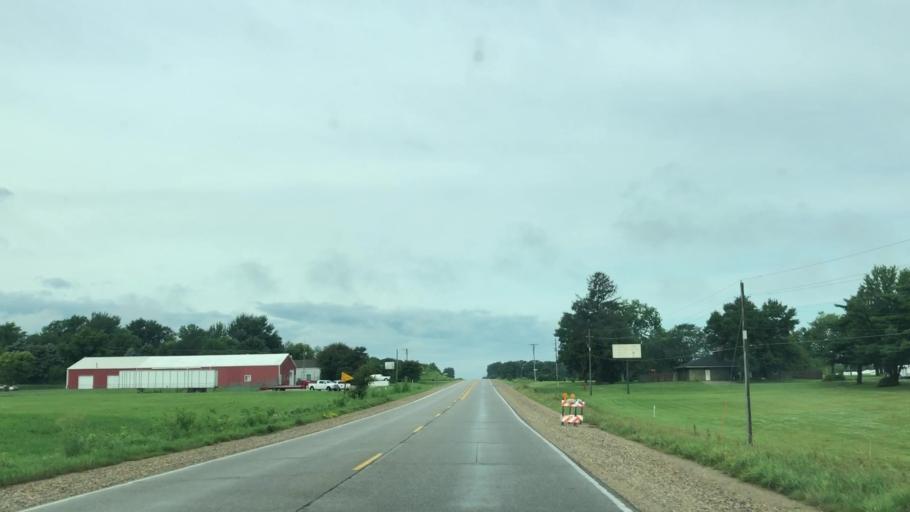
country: US
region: Iowa
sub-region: Marshall County
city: Marshalltown
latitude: 42.0075
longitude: -92.9384
